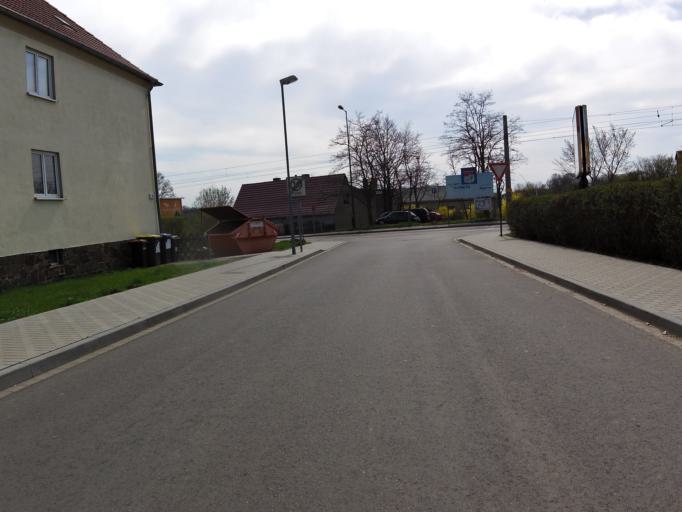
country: DE
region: Saxony
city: Schkeuditz
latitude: 51.3843
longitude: 12.2794
